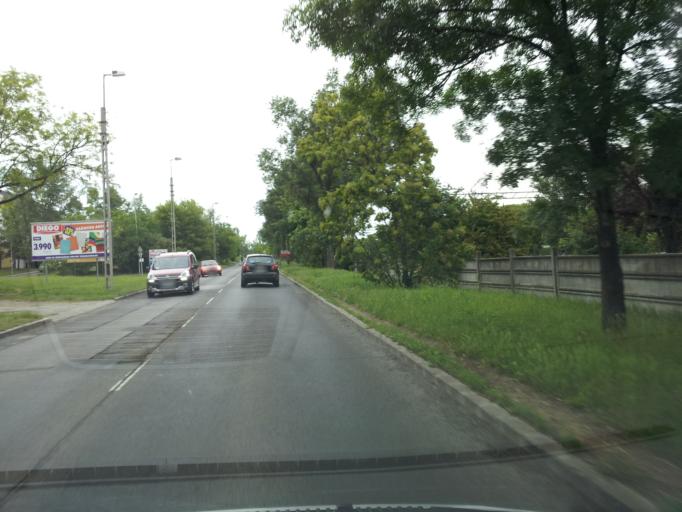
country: HU
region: Pest
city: Budakalasz
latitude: 47.6007
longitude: 19.0561
